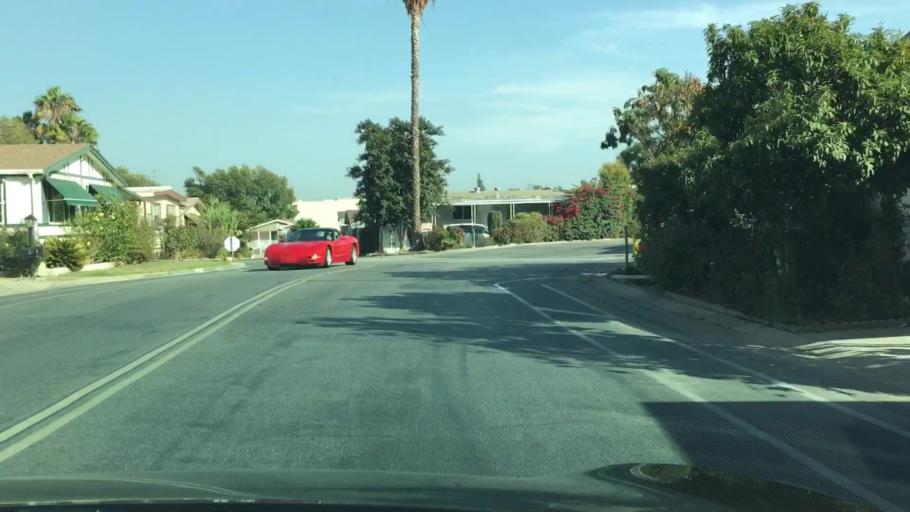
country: US
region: California
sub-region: Los Angeles County
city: Avocado Heights
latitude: 34.0262
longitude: -117.9912
